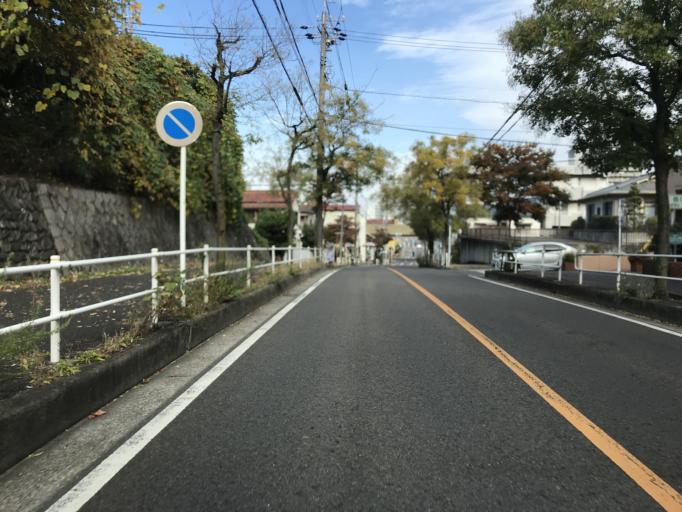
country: JP
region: Aichi
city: Nagoya-shi
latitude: 35.1872
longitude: 136.9242
